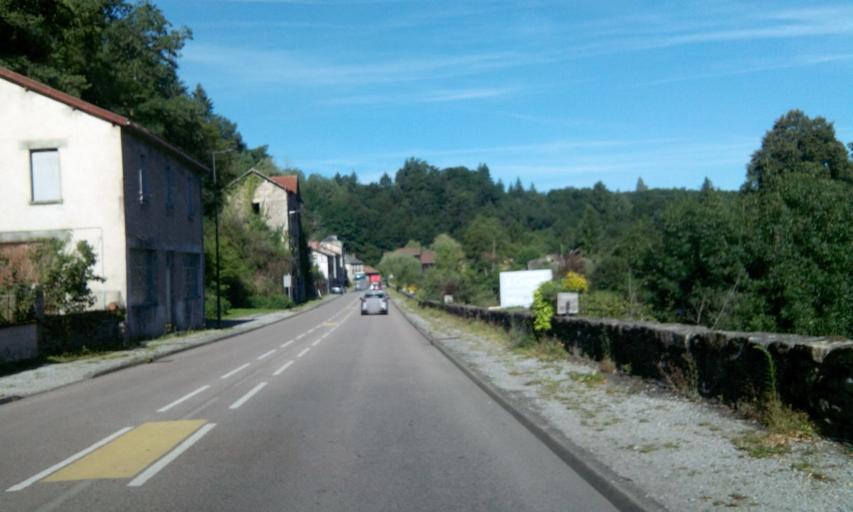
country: FR
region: Limousin
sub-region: Departement de la Haute-Vienne
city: Saint-Leonard-de-Noblat
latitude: 45.8342
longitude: 1.4768
